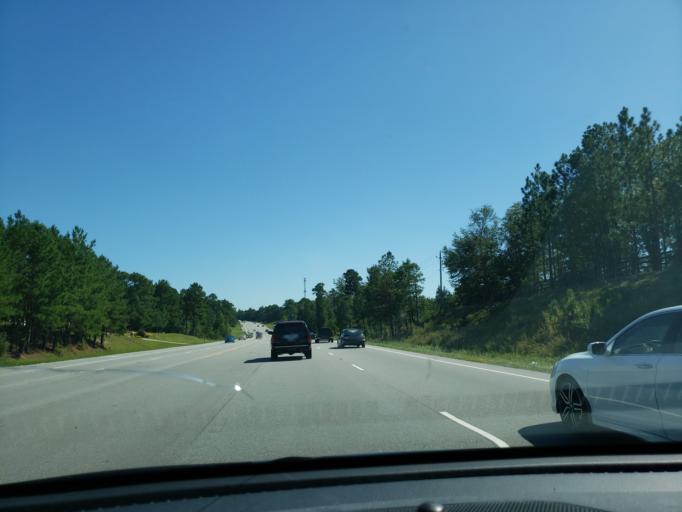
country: US
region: North Carolina
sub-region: Lee County
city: Broadway
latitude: 35.3518
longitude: -79.1088
